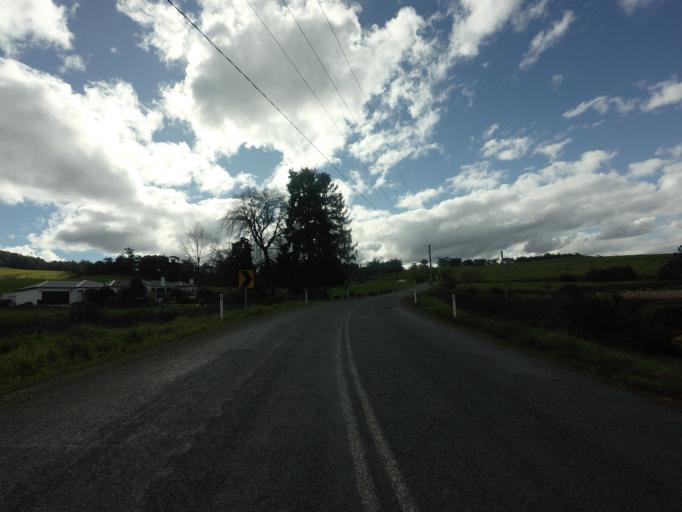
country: AU
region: Tasmania
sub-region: Huon Valley
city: Geeveston
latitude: -43.2041
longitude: 146.9654
